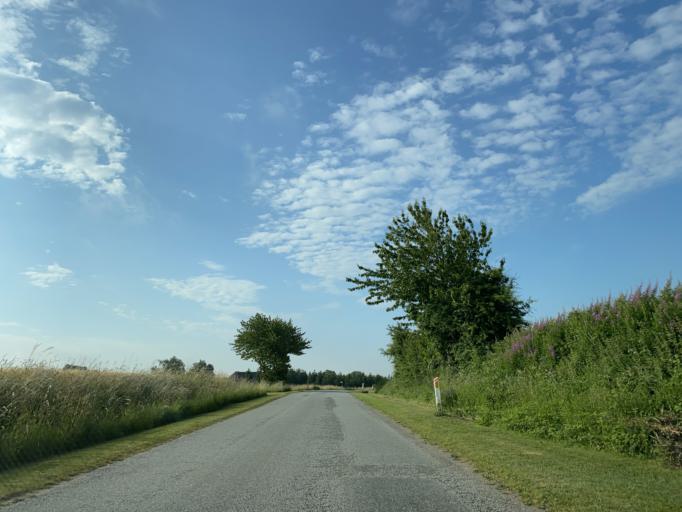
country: DK
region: South Denmark
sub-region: Haderslev Kommune
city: Haderslev
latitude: 55.1815
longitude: 9.4808
